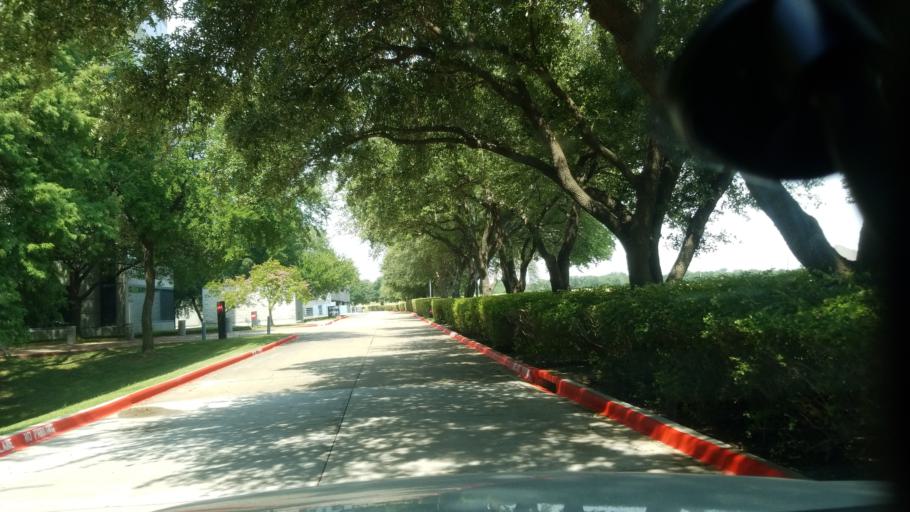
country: US
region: Texas
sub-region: Dallas County
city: Farmers Branch
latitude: 32.9107
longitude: -96.9269
